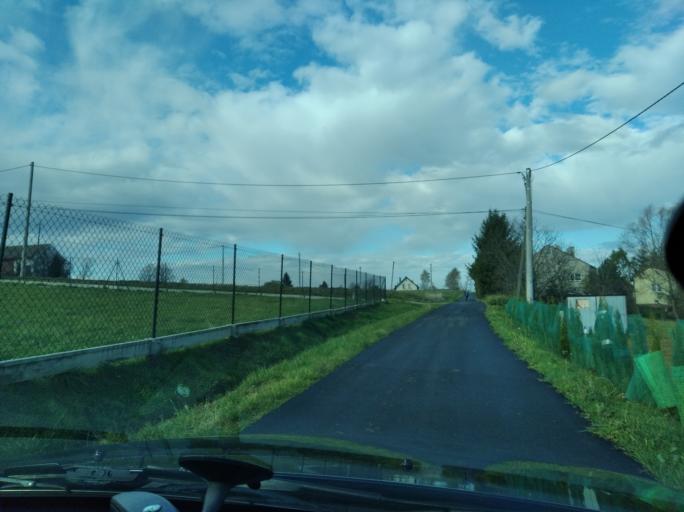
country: PL
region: Subcarpathian Voivodeship
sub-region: Powiat debicki
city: Debica
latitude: 50.0267
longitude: 21.4652
